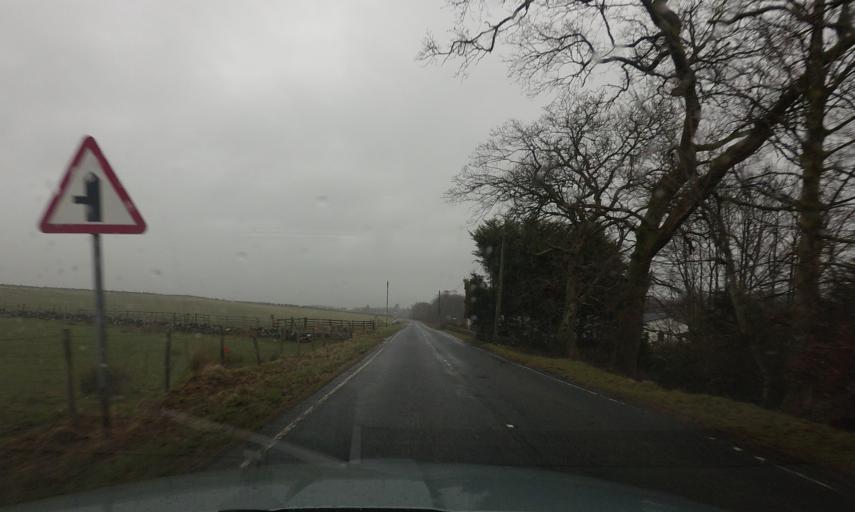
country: GB
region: Scotland
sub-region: Stirling
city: Balfron
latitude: 56.1041
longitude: -4.3583
